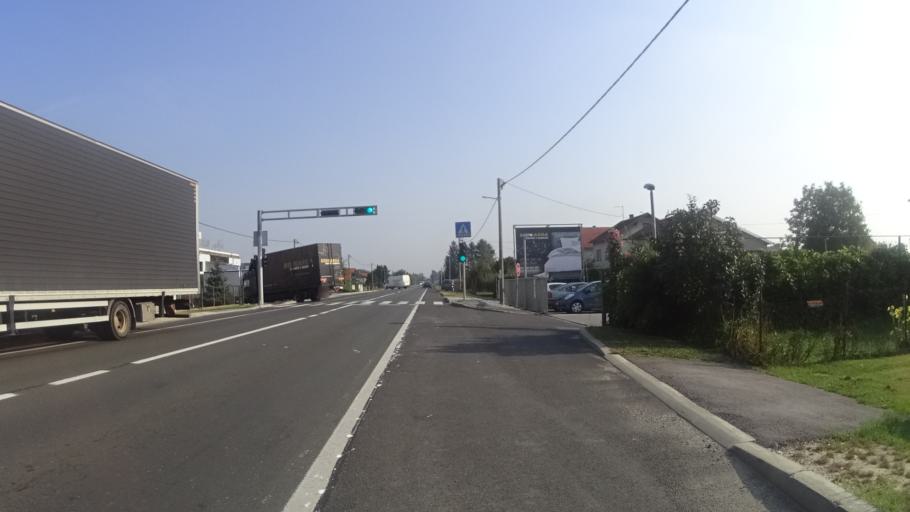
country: HR
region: Varazdinska
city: Varazdin
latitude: 46.3376
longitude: 16.3613
